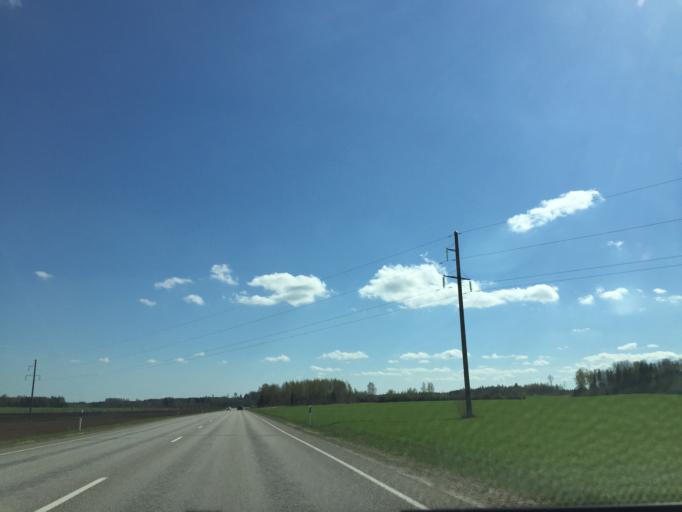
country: EE
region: Valgamaa
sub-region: Valga linn
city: Valga
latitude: 57.8809
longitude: 26.0595
